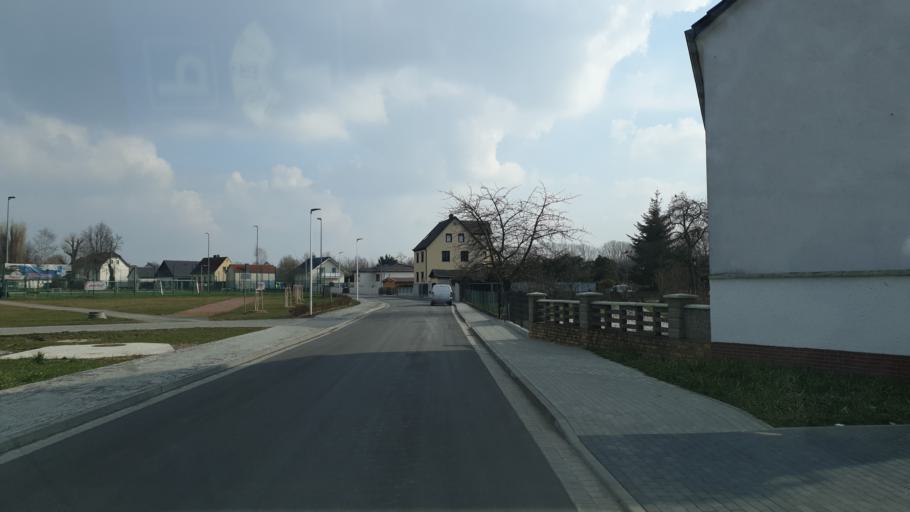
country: DE
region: Saxony
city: Wiedemar
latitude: 51.4434
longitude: 12.2255
